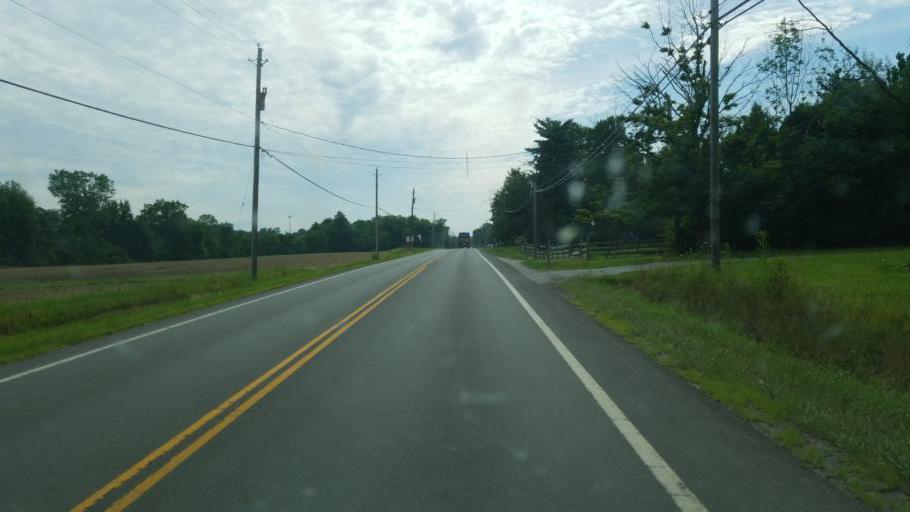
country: US
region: Ohio
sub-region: Cuyahoga County
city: Olmsted Falls
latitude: 41.3125
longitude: -81.9103
